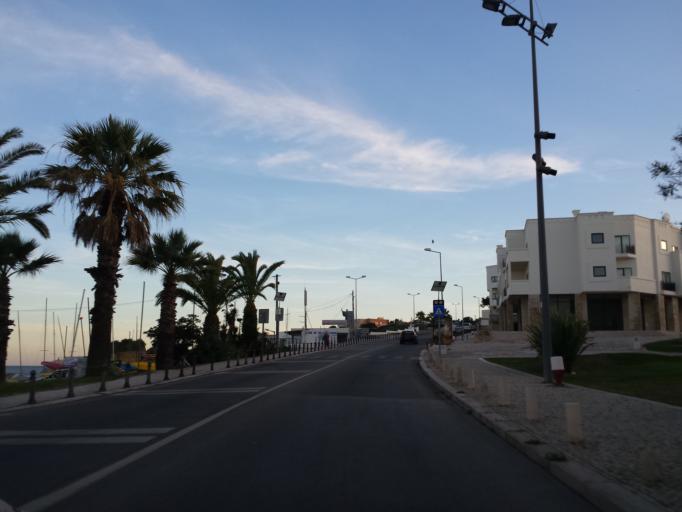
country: PT
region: Faro
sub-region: Lagos
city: Lagos
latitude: 37.0992
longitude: -8.6689
